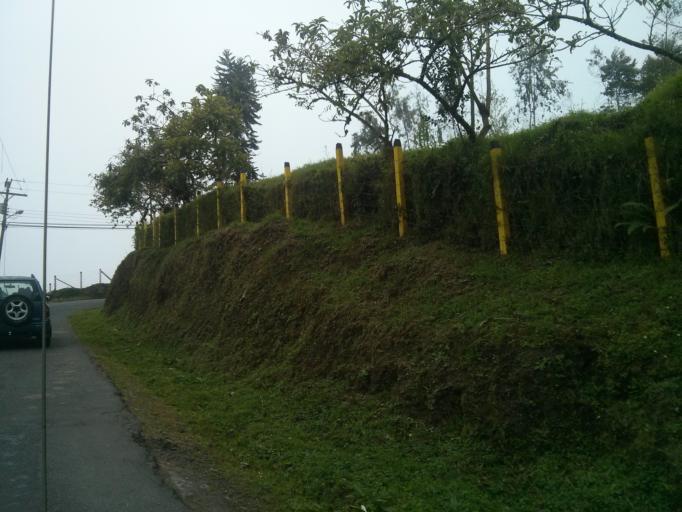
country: CR
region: San Jose
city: Ipis
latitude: 10.0078
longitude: -83.9549
